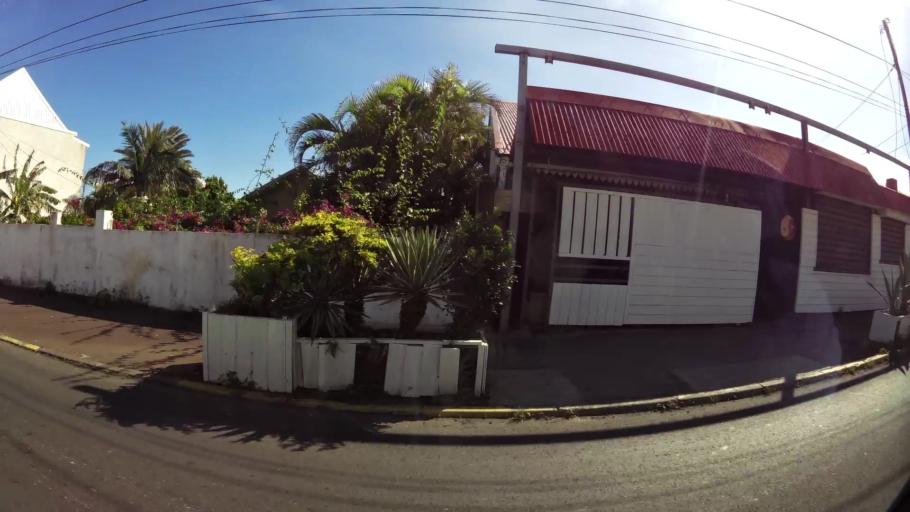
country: RE
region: Reunion
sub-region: Reunion
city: Saint-Pierre
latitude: -21.3418
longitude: 55.4686
